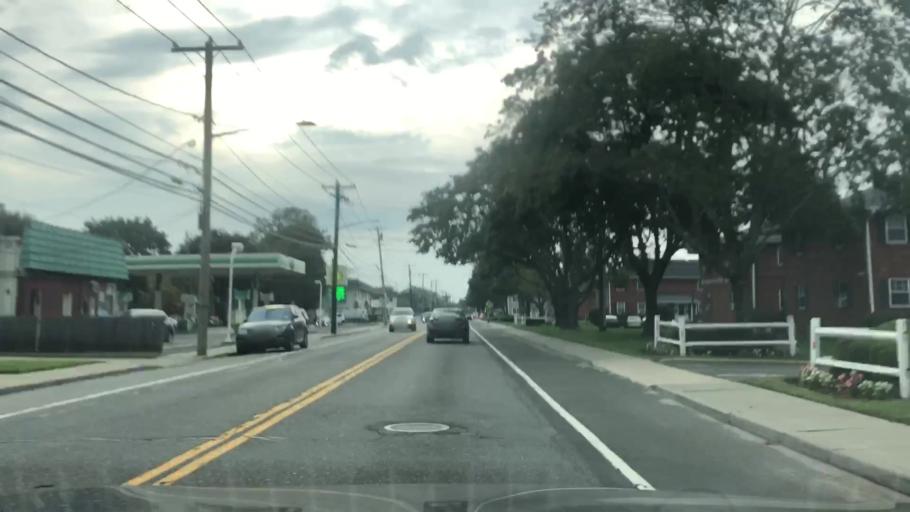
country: US
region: New York
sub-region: Nassau County
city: North Bellmore
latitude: 40.6913
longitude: -73.5375
